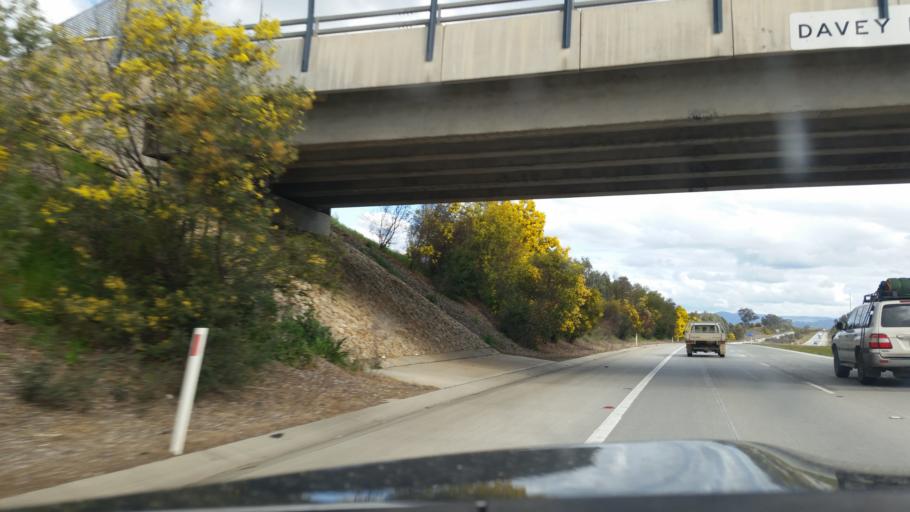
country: AU
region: New South Wales
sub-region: Albury Municipality
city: Lavington
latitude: -36.0015
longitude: 146.9921
